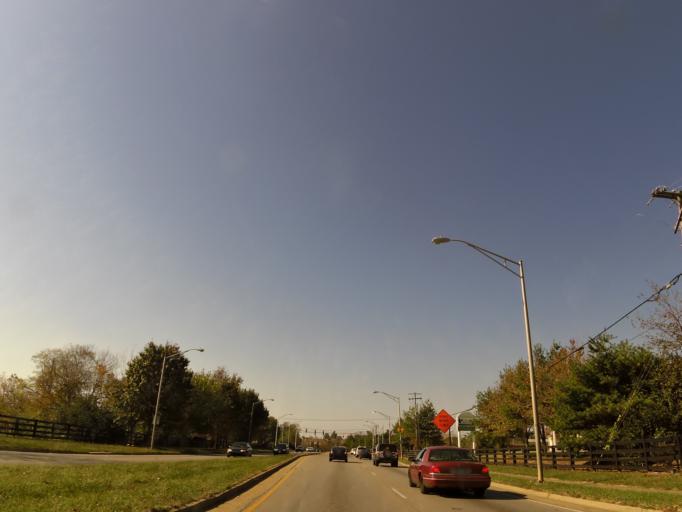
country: US
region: Kentucky
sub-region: Fayette County
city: Lexington
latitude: 38.0068
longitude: -84.4339
